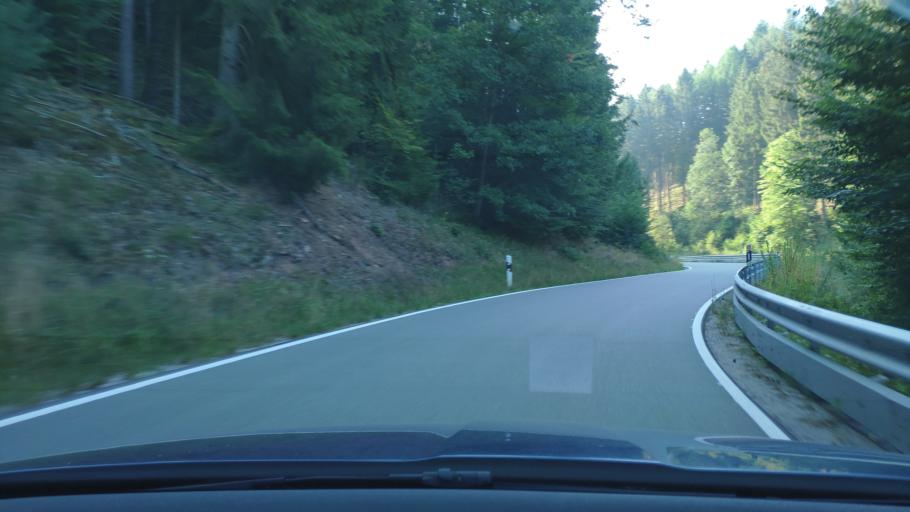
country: DE
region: Rheinland-Pfalz
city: Ludwigswinkel
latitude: 49.1027
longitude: 7.6224
